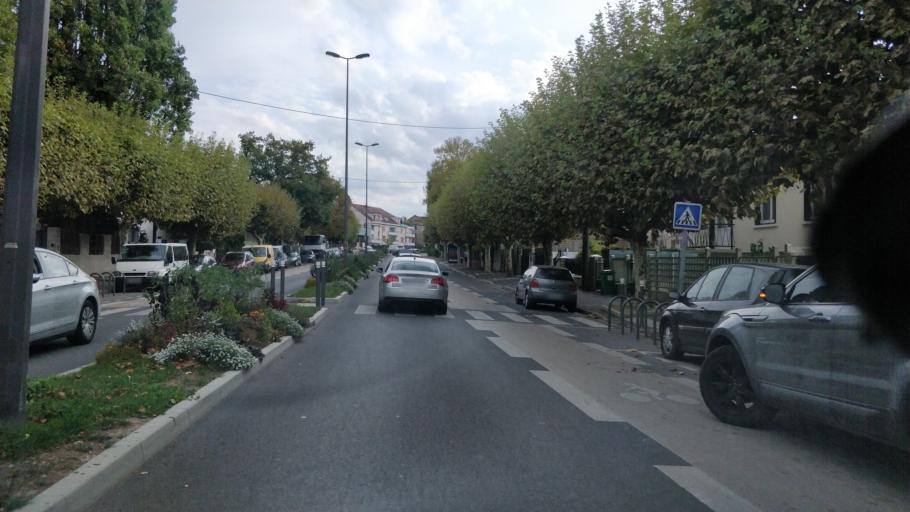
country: FR
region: Ile-de-France
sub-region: Departement de Seine-Saint-Denis
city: Clichy-sous-Bois
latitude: 48.9005
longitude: 2.5467
